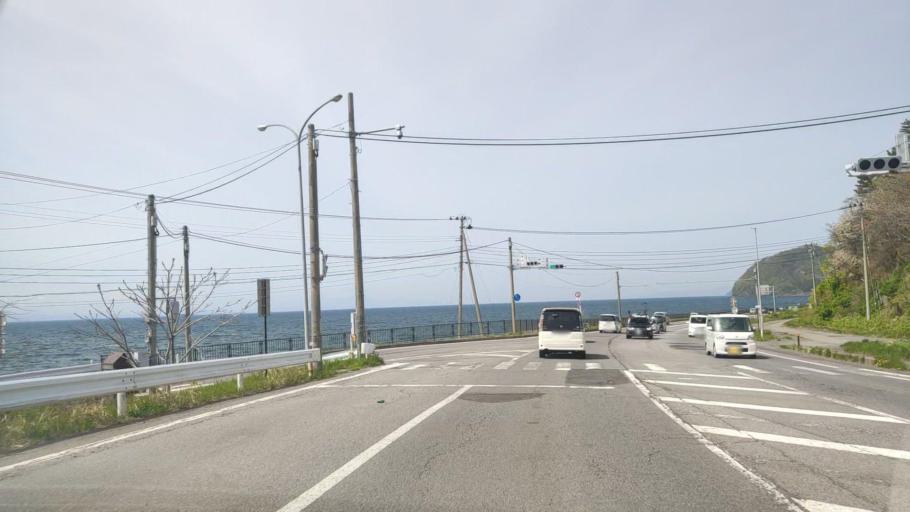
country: JP
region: Aomori
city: Aomori Shi
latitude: 40.8773
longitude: 140.8501
